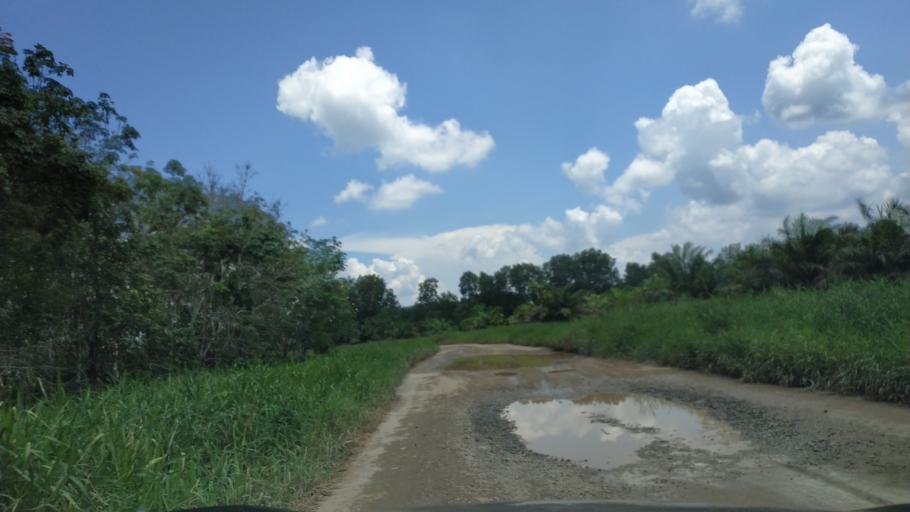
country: ID
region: Riau
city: Pangkalanbunut
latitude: 0.1945
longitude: 102.3856
